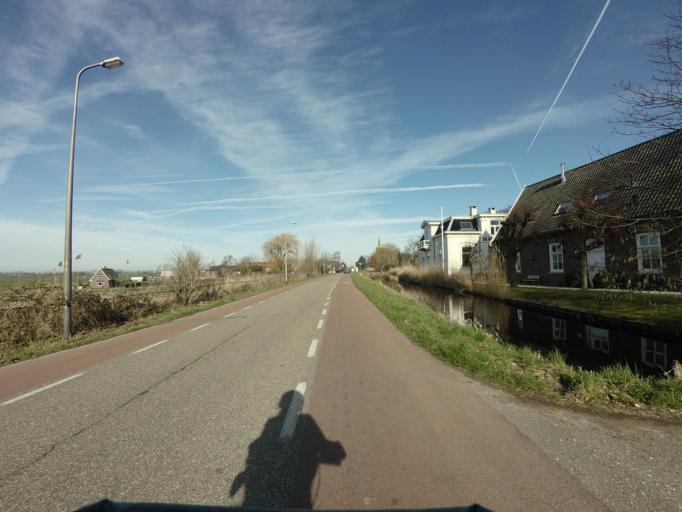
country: NL
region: South Holland
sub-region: Gemeente Kaag en Braassem
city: Leimuiden
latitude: 52.2087
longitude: 4.6686
